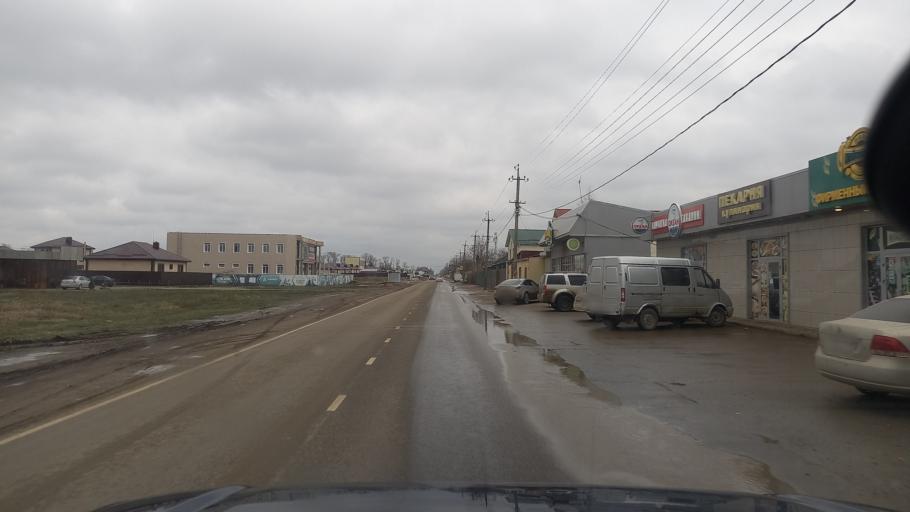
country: RU
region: Krasnodarskiy
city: Pashkovskiy
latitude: 45.0593
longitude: 39.1673
